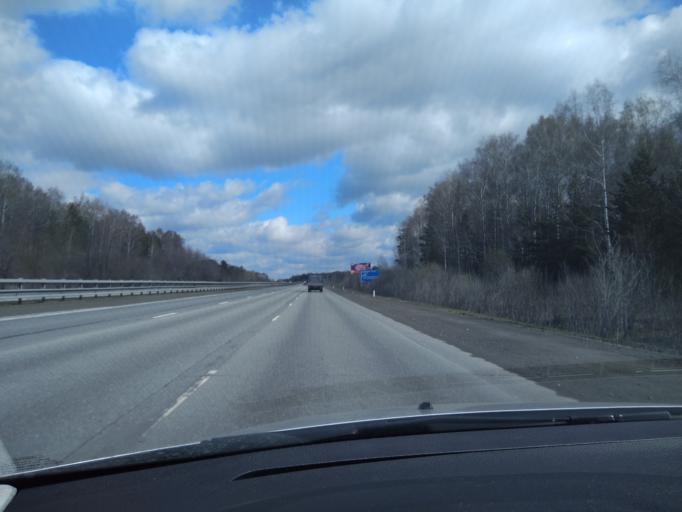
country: RU
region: Sverdlovsk
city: Sredneuralsk
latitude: 56.9771
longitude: 60.5195
